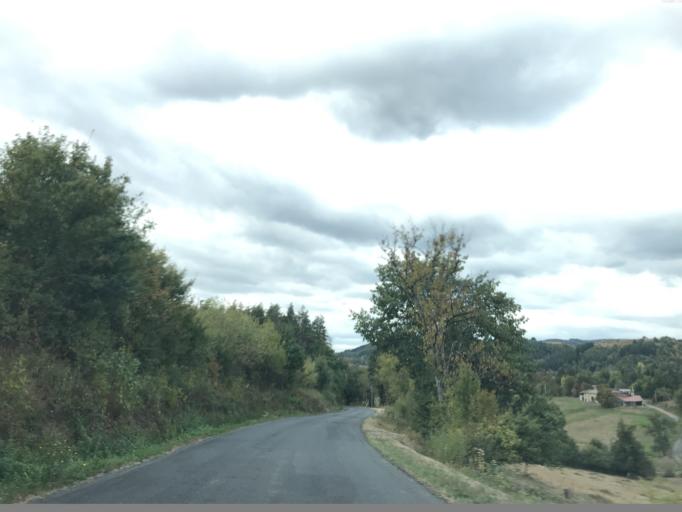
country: FR
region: Auvergne
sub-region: Departement du Puy-de-Dome
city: Escoutoux
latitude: 45.7791
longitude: 3.5909
